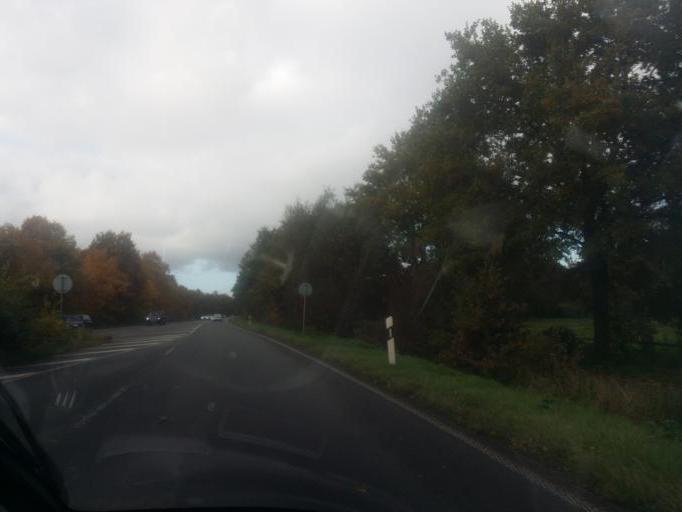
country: DE
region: Schleswig-Holstein
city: Rellingen
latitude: 53.6103
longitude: 9.8086
